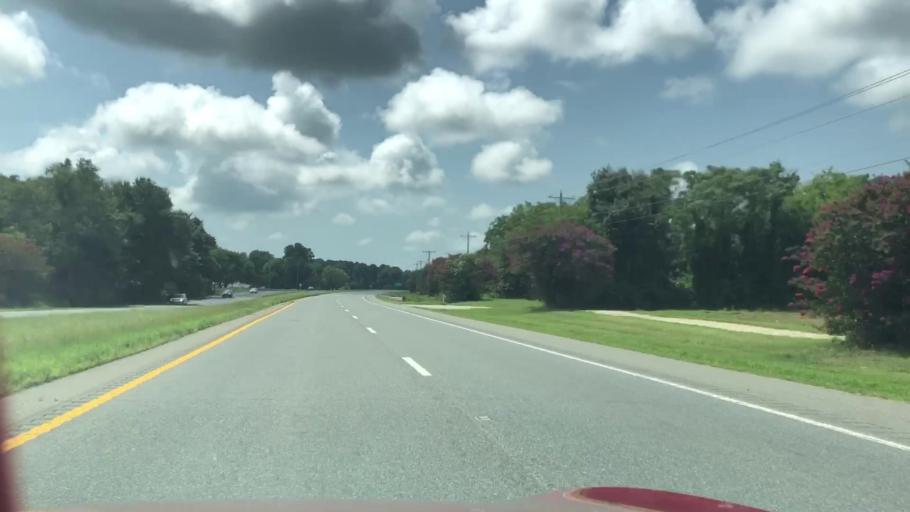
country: US
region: Virginia
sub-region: Northampton County
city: Eastville
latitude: 37.3013
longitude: -75.9681
